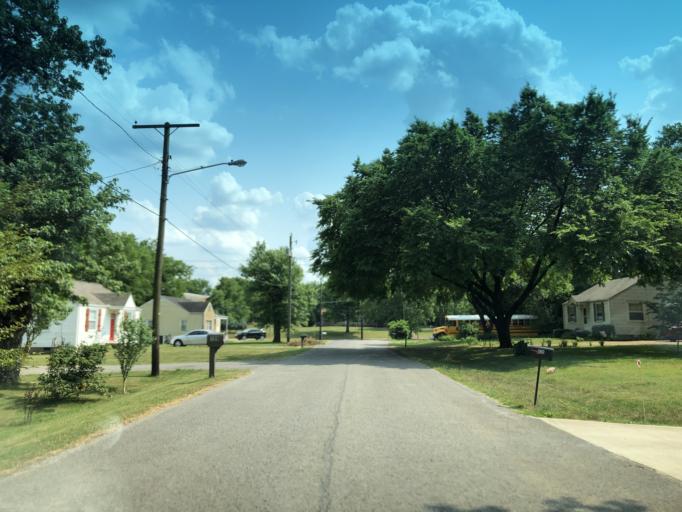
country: US
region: Tennessee
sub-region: Davidson County
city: Goodlettsville
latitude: 36.2619
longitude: -86.7170
